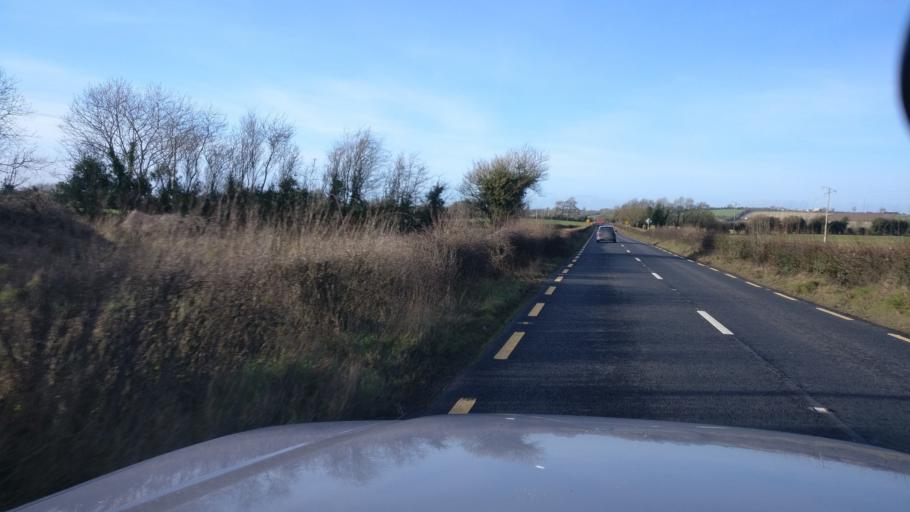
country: IE
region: Leinster
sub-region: Laois
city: Mountmellick
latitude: 53.1840
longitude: -7.3987
